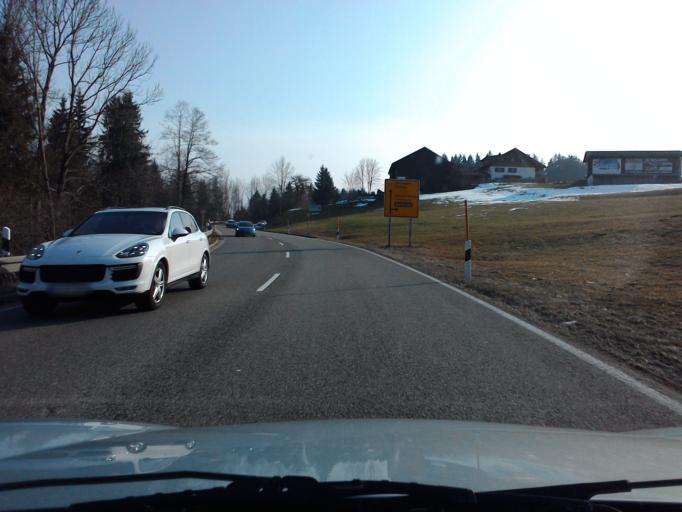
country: DE
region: Bavaria
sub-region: Swabia
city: Sonthofen
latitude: 47.4875
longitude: 10.2669
